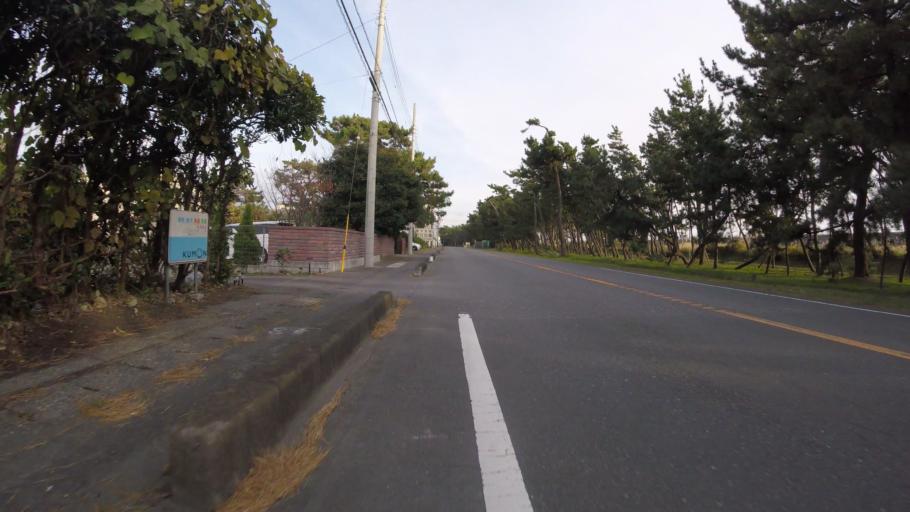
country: JP
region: Shizuoka
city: Fuji
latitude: 35.1321
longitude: 138.7590
